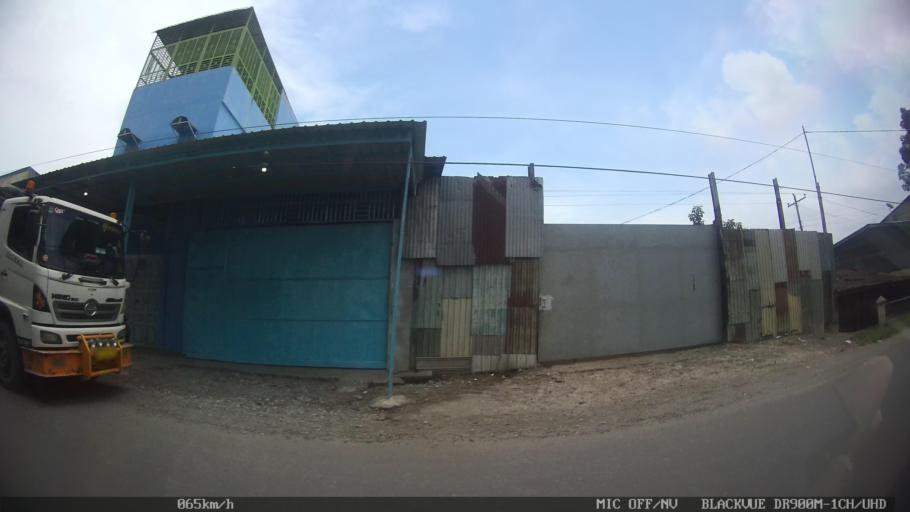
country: ID
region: North Sumatra
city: Labuhan Deli
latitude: 3.6942
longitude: 98.6728
